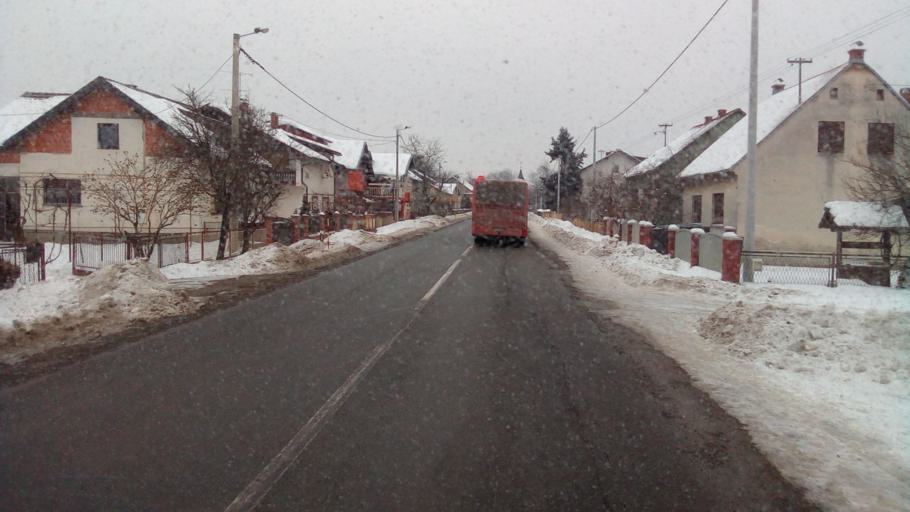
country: HR
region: Sisacko-Moslavacka
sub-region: Grad Sisak
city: Sisak
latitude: 45.4390
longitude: 16.3521
